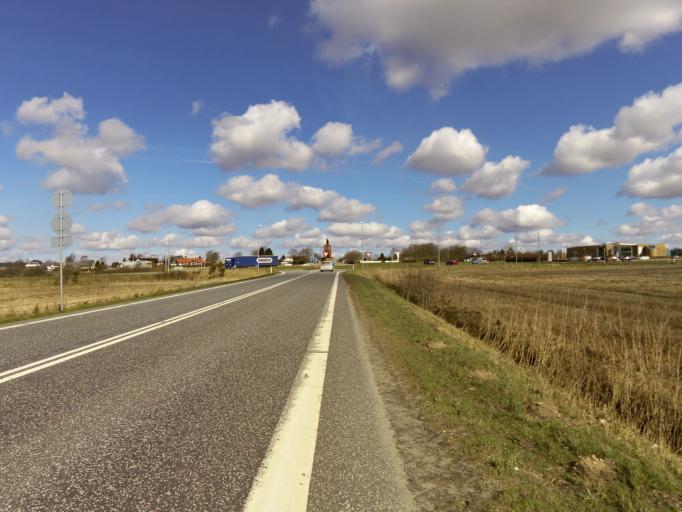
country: DK
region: South Denmark
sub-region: Tonder Kommune
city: Toftlund
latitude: 55.1790
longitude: 9.0620
